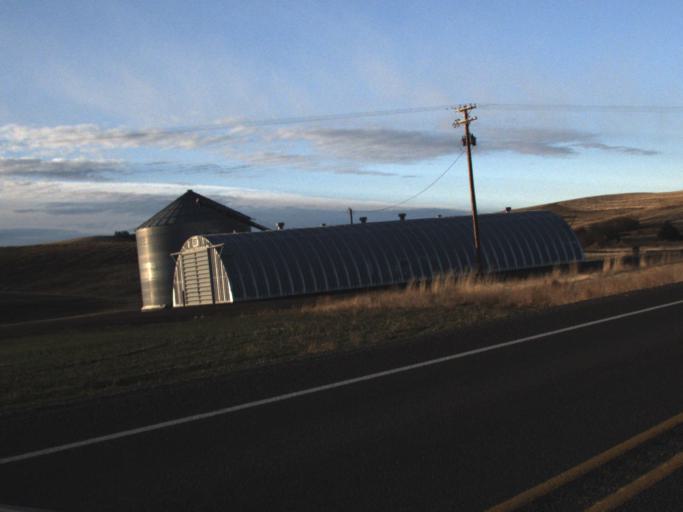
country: US
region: Washington
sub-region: Garfield County
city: Pomeroy
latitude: 46.7369
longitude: -117.7333
